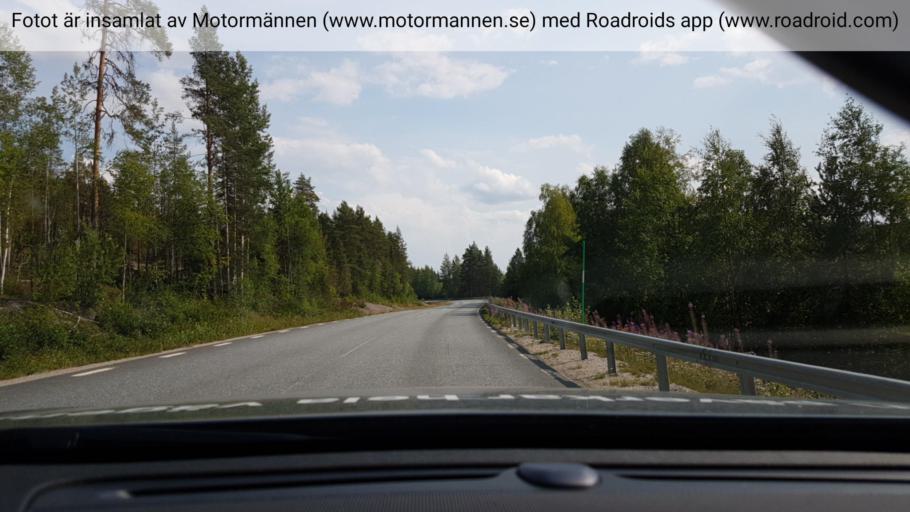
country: SE
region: Vaesterbotten
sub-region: Lycksele Kommun
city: Lycksele
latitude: 64.4062
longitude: 19.0284
